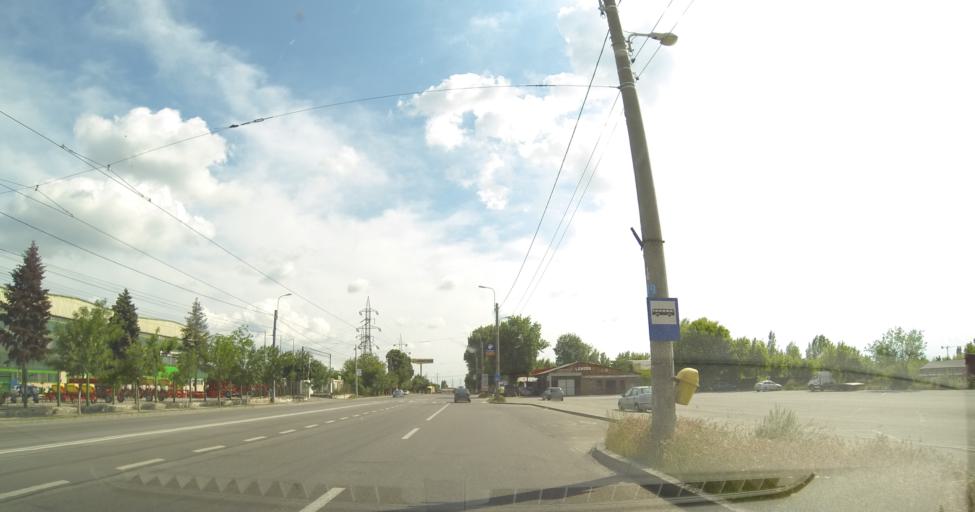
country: RO
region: Dolj
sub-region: Municipiul Craiova
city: Facai
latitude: 44.3024
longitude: 23.8326
